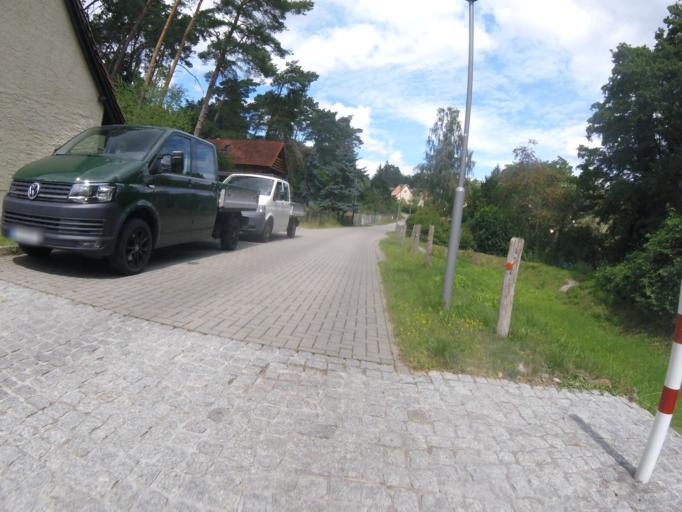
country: DE
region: Brandenburg
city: Bestensee
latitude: 52.2587
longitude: 13.6050
